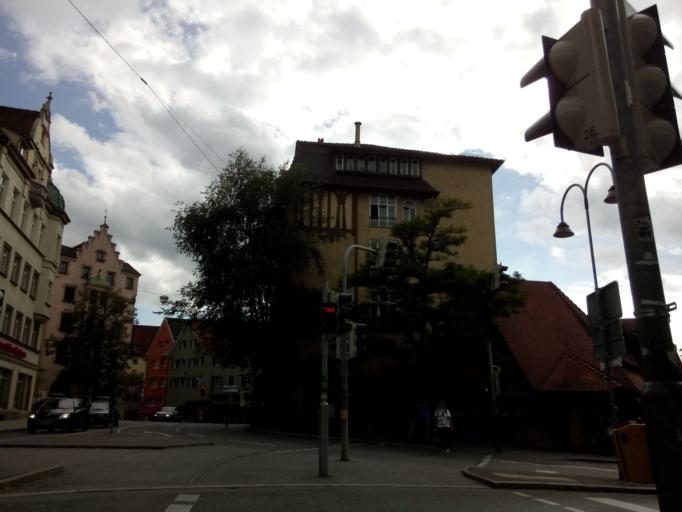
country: DE
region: Baden-Wuerttemberg
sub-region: Tuebingen Region
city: Tuebingen
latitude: 48.5221
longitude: 9.0579
